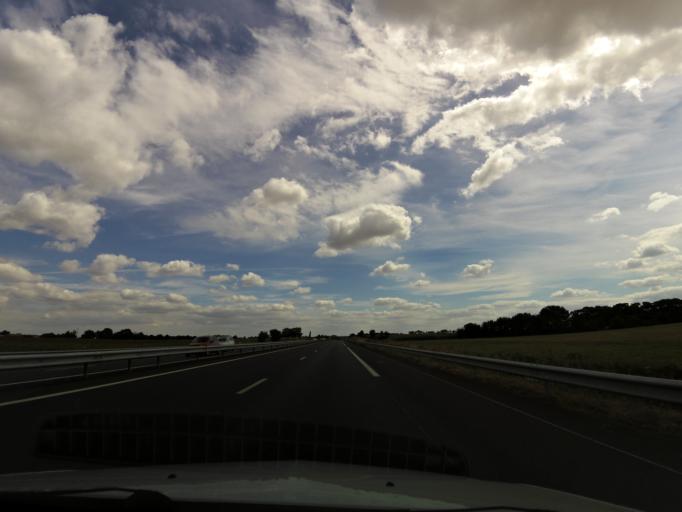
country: FR
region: Pays de la Loire
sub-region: Departement de la Vendee
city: Bouffere
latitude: 46.9268
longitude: -1.3353
